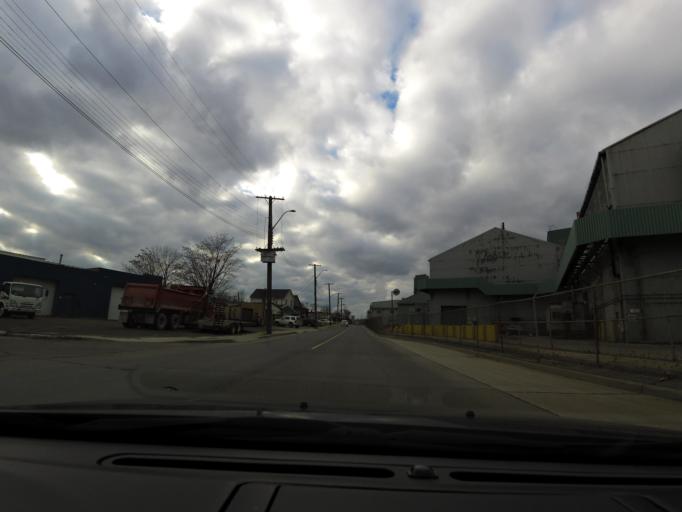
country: CA
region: Ontario
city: Hamilton
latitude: 43.2560
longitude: -79.8057
